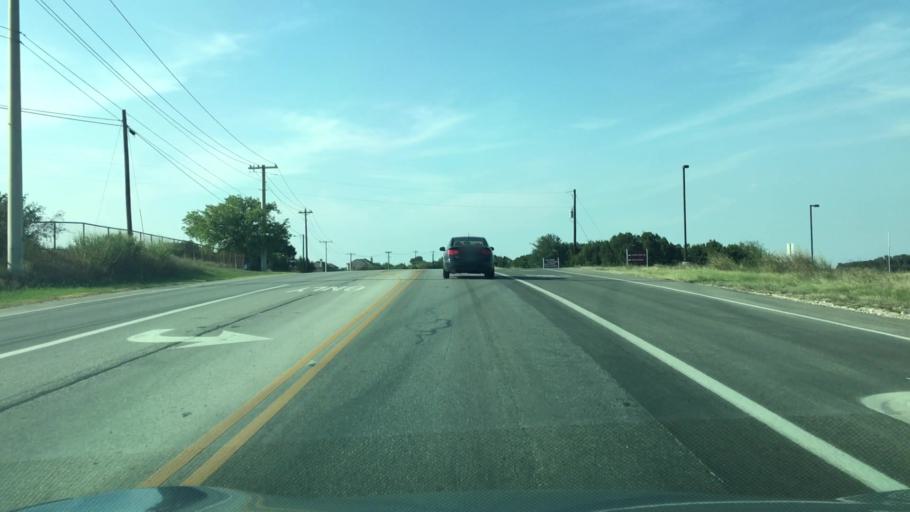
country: US
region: Texas
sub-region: Hays County
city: Dripping Springs
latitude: 30.1797
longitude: -98.0020
